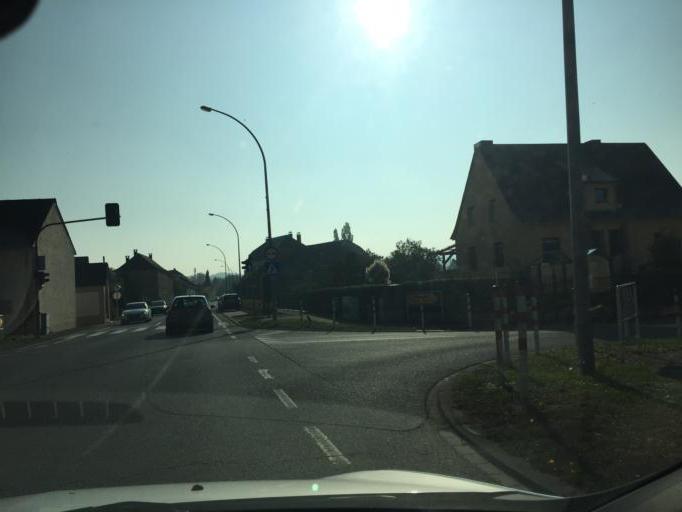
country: LU
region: Grevenmacher
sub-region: Canton de Remich
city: Bous
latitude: 49.5548
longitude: 6.3133
